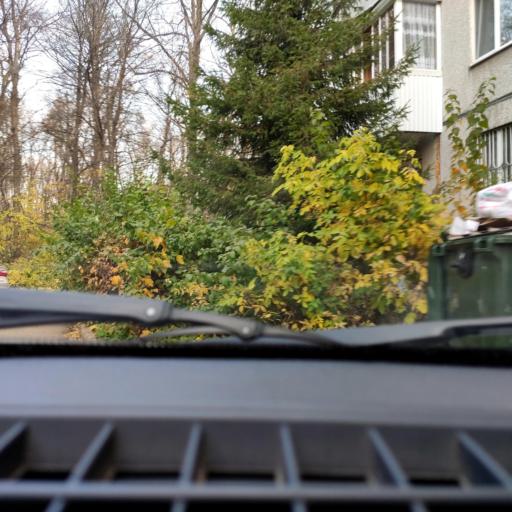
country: RU
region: Bashkortostan
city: Ufa
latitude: 54.7948
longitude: 56.0469
